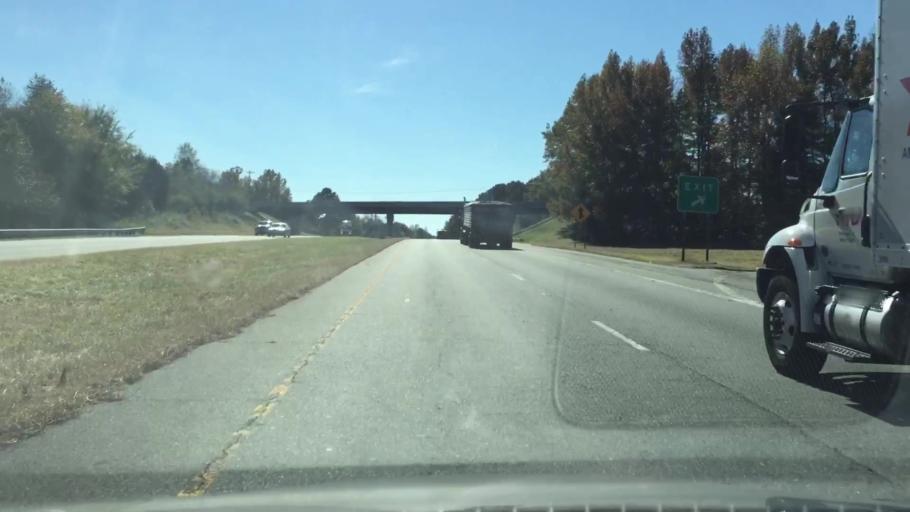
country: US
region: North Carolina
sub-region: Guilford County
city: McLeansville
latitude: 36.2277
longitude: -79.6784
